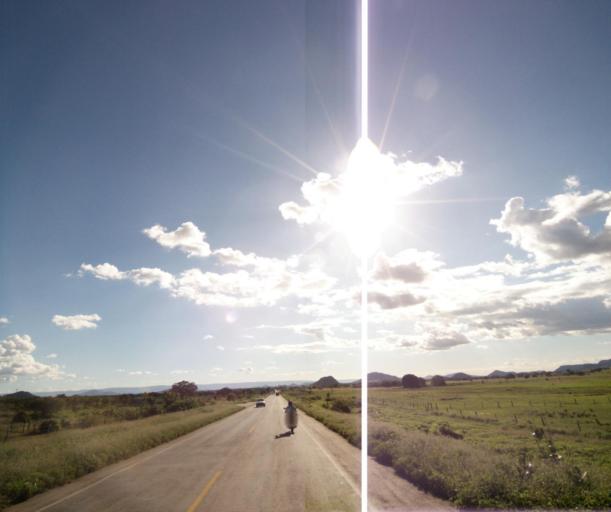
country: BR
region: Bahia
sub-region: Guanambi
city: Guanambi
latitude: -14.1573
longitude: -42.7077
